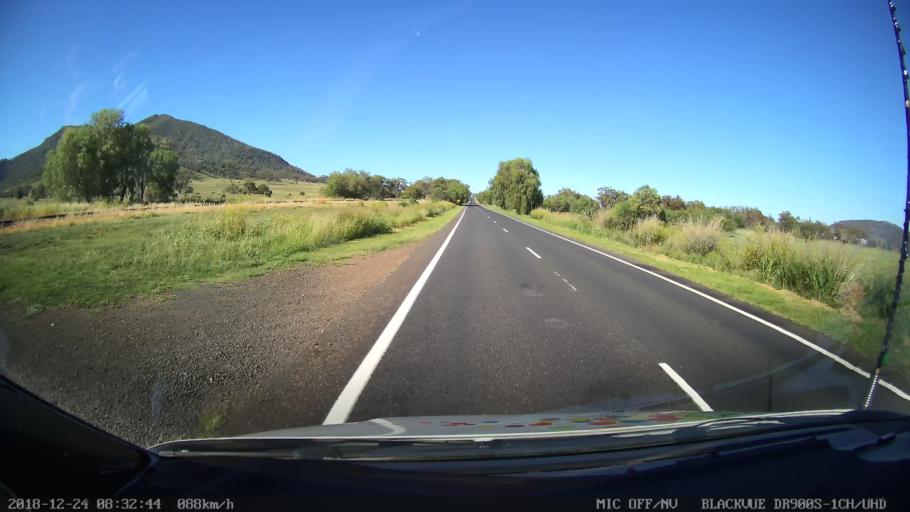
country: AU
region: New South Wales
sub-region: Tamworth Municipality
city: Phillip
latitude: -31.2819
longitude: 150.6940
